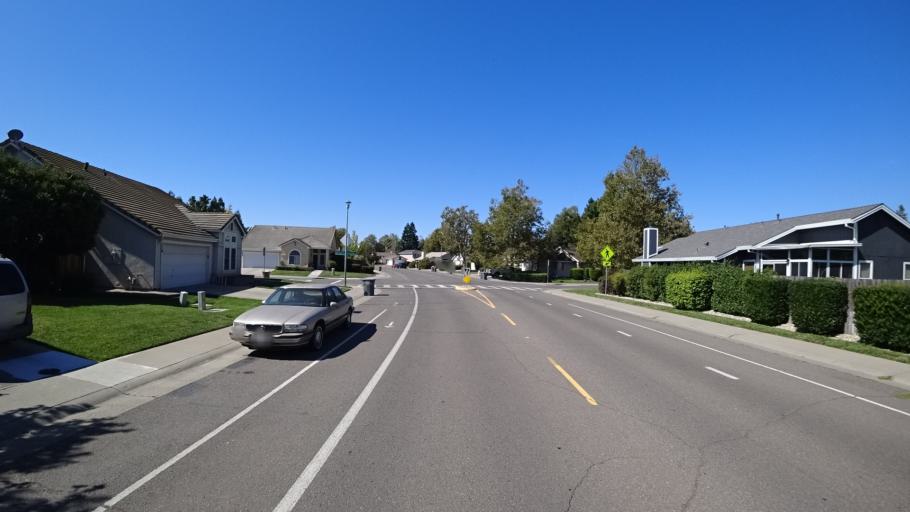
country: US
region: California
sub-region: Sacramento County
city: Laguna
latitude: 38.4284
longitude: -121.4238
